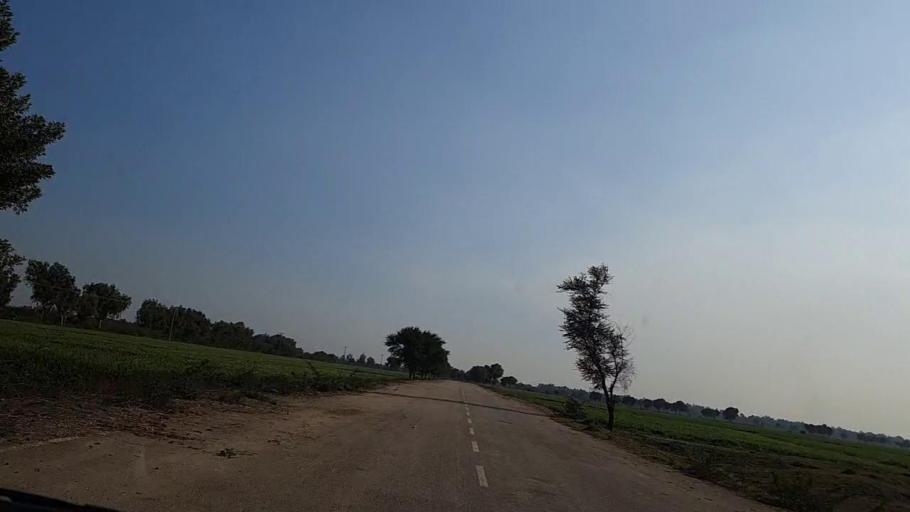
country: PK
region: Sindh
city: Sakrand
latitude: 26.1221
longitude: 68.2484
